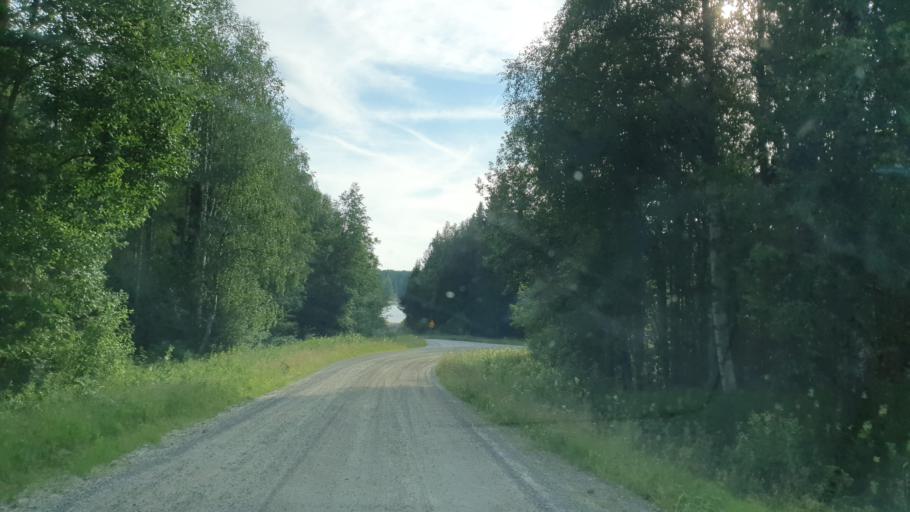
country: FI
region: Kainuu
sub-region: Kehys-Kainuu
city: Kuhmo
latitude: 64.2441
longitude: 29.4884
